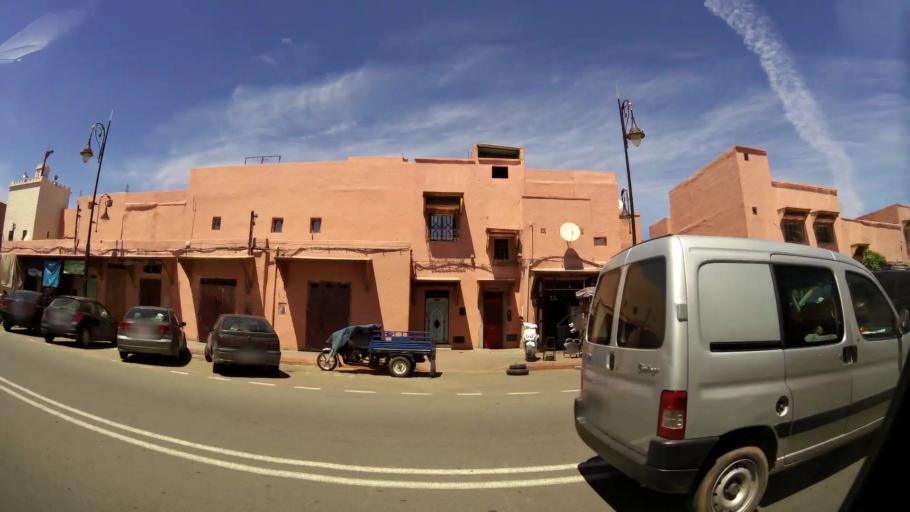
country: MA
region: Marrakech-Tensift-Al Haouz
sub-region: Marrakech
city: Marrakesh
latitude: 31.6142
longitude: -7.9785
